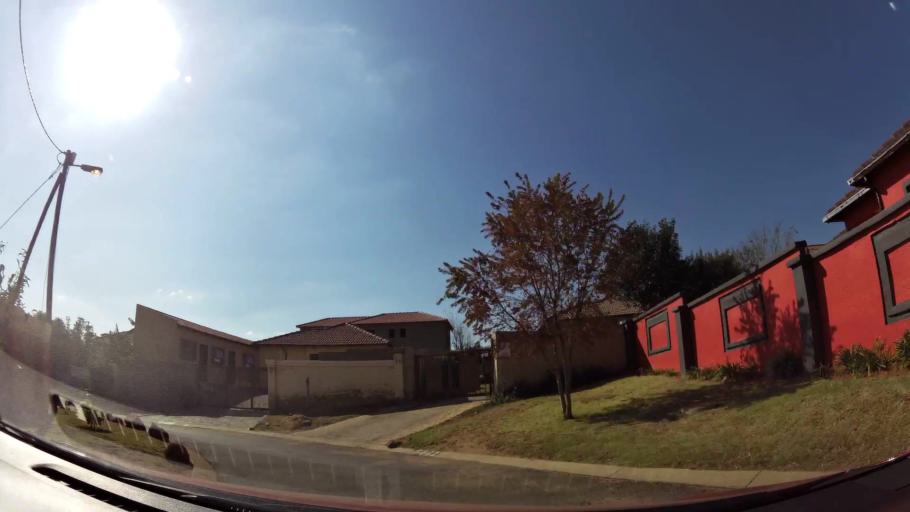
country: ZA
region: Gauteng
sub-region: West Rand District Municipality
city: Muldersdriseloop
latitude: -26.0297
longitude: 27.9390
